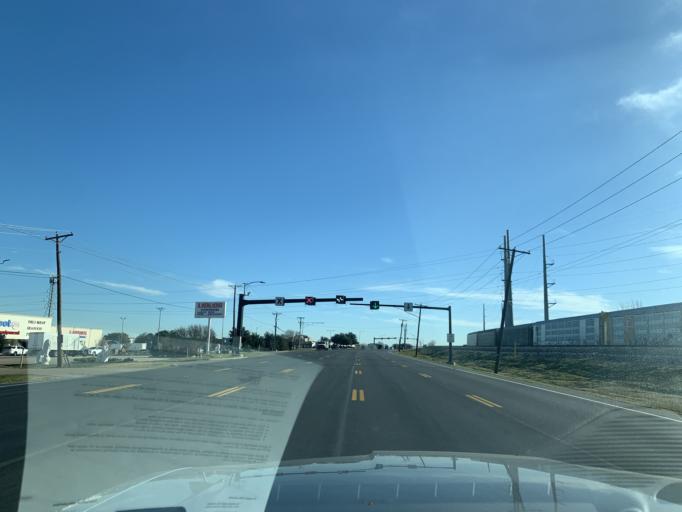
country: US
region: Texas
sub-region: Tarrant County
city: Arlington
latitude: 32.7428
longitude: -97.0757
